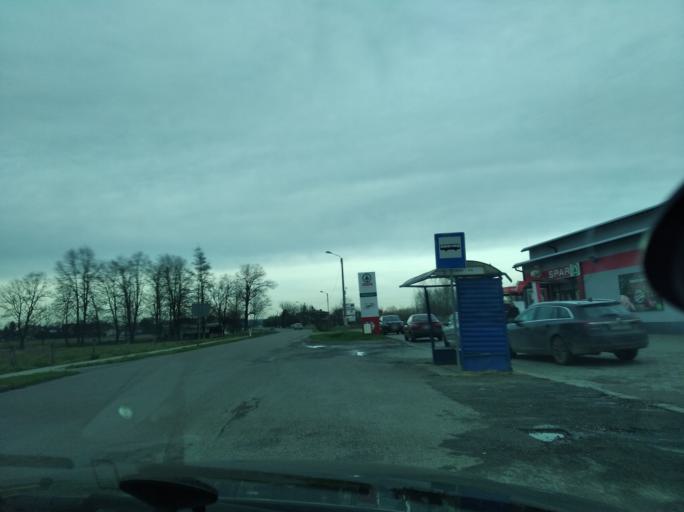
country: PL
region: Subcarpathian Voivodeship
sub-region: Powiat lancucki
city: Czarna
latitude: 50.0946
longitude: 22.1853
